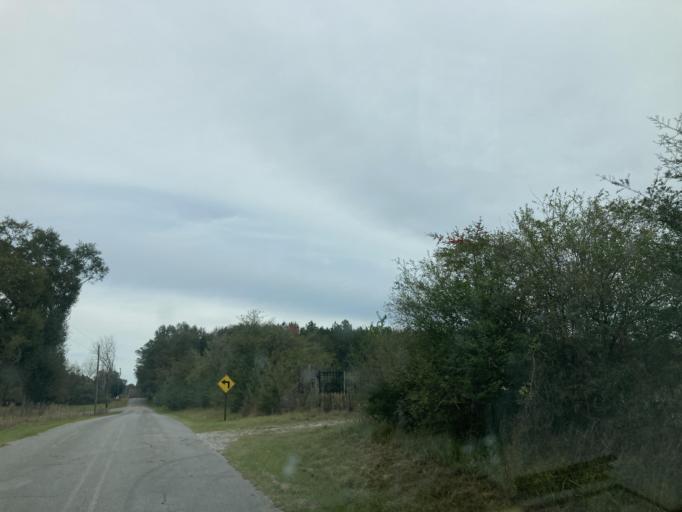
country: US
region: Mississippi
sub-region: Lamar County
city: Lumberton
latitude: 31.0490
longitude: -89.4505
